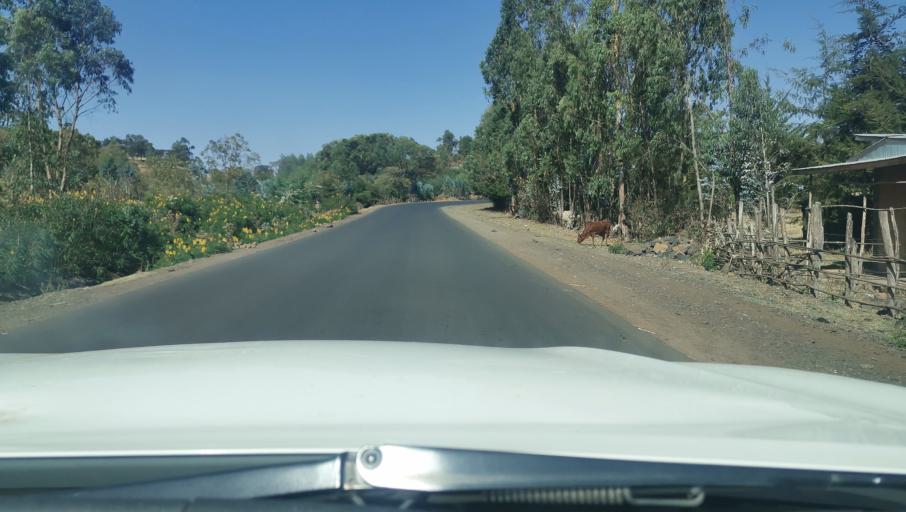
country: ET
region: Oromiya
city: Gedo
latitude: 8.9660
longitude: 37.5247
